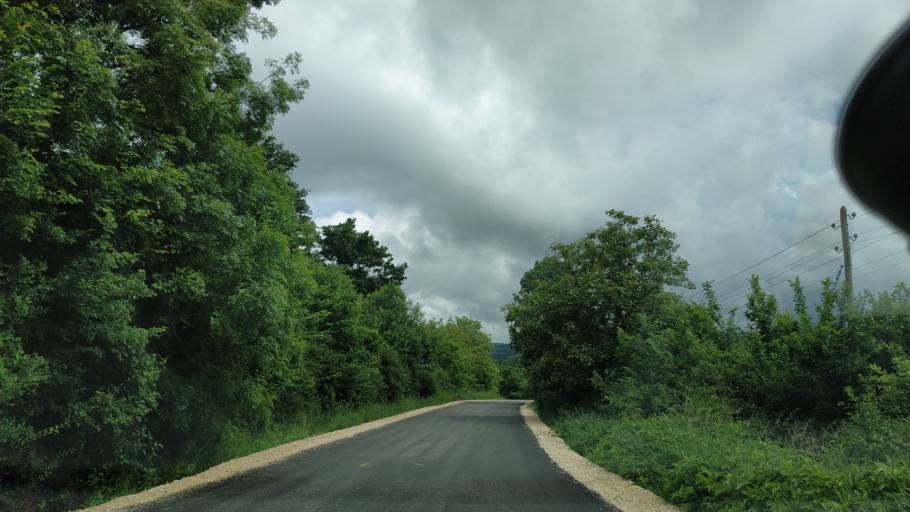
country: RS
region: Central Serbia
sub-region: Zajecarski Okrug
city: Soko Banja
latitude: 43.6526
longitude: 21.9025
